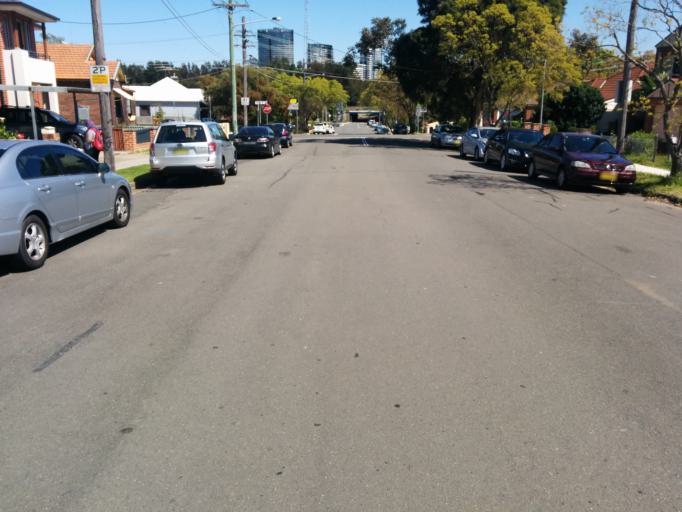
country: AU
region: New South Wales
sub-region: Canada Bay
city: Concord West
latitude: -33.8478
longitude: 151.0847
